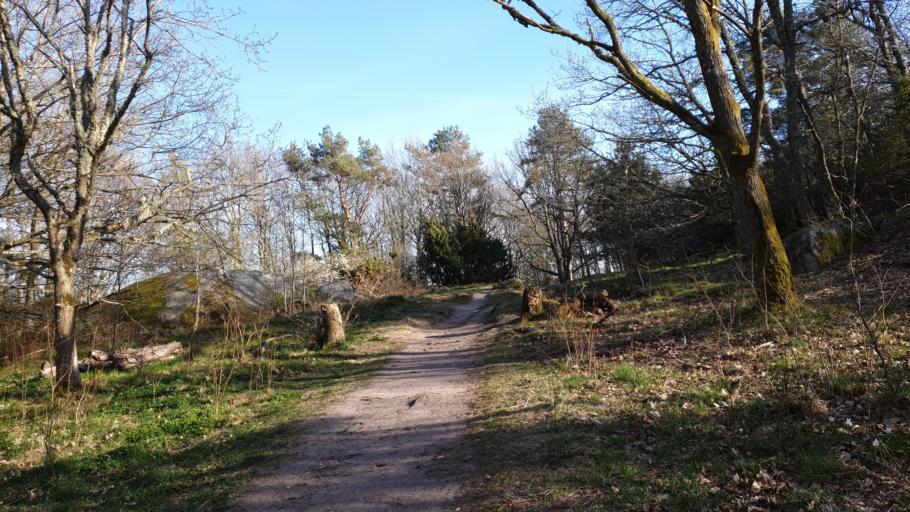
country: SE
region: Vaestra Goetaland
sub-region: Goteborg
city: Billdal
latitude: 57.5909
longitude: 11.9178
